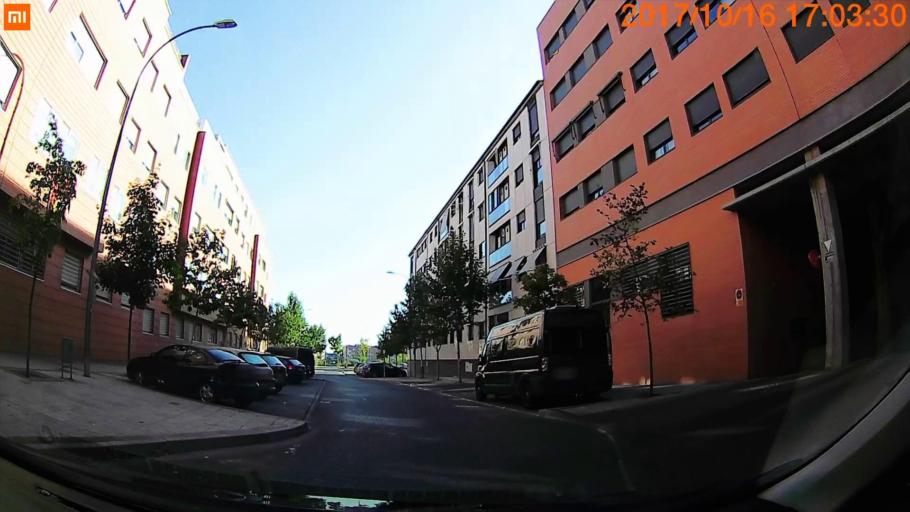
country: ES
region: Madrid
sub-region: Provincia de Madrid
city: Alcobendas
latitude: 40.5560
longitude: -3.6608
